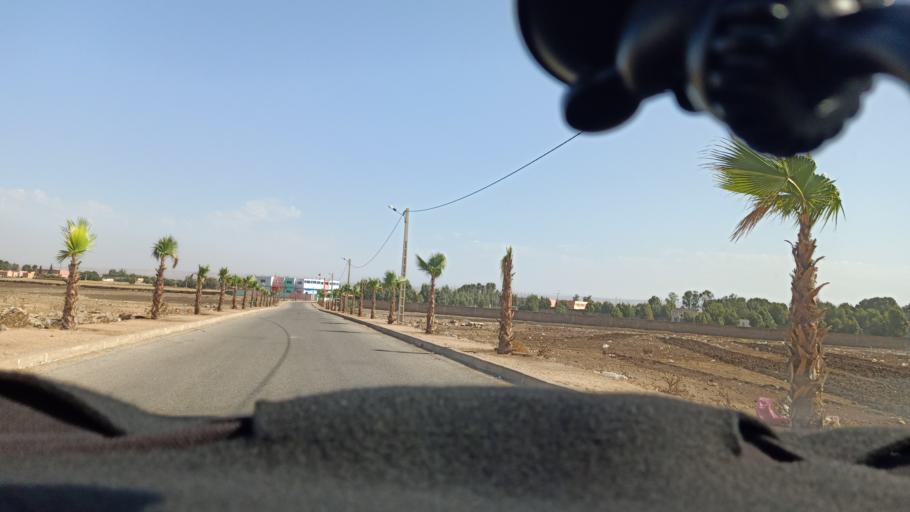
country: MA
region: Doukkala-Abda
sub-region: Safi
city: Youssoufia
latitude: 32.3504
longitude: -8.8357
